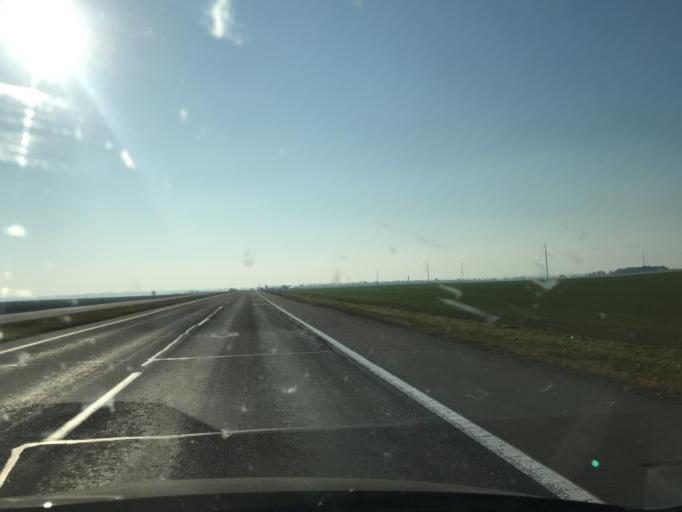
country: BY
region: Minsk
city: Haradzyeya
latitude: 53.3628
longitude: 26.4791
